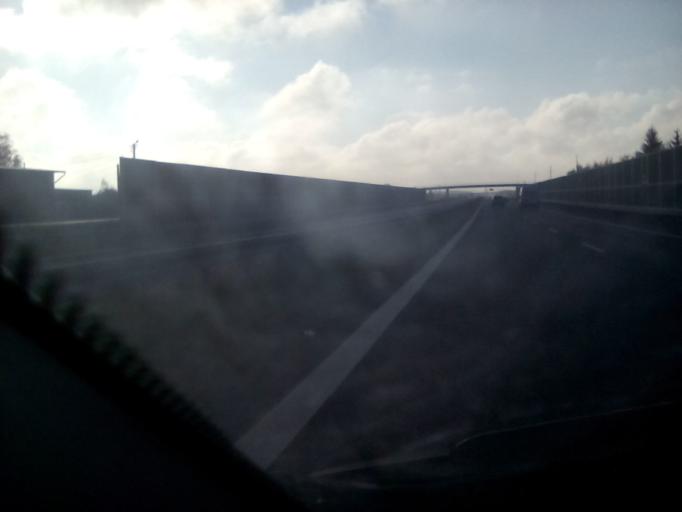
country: PL
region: Masovian Voivodeship
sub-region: Powiat grojecki
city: Goszczyn
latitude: 51.7727
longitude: 20.8989
